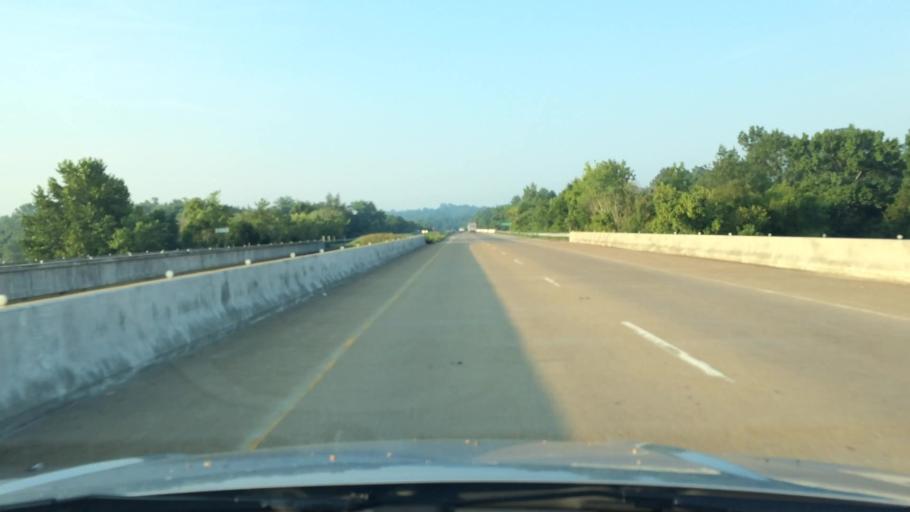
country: US
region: Tennessee
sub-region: Giles County
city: Pulaski
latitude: 35.1986
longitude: -87.0637
